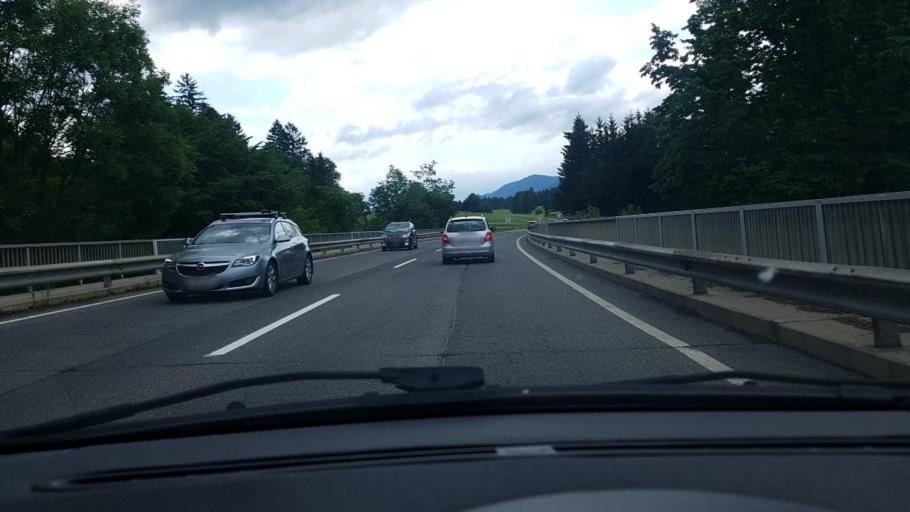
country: AT
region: Carinthia
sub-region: Politischer Bezirk Villach Land
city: Stockenboi
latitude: 46.6269
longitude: 13.4836
